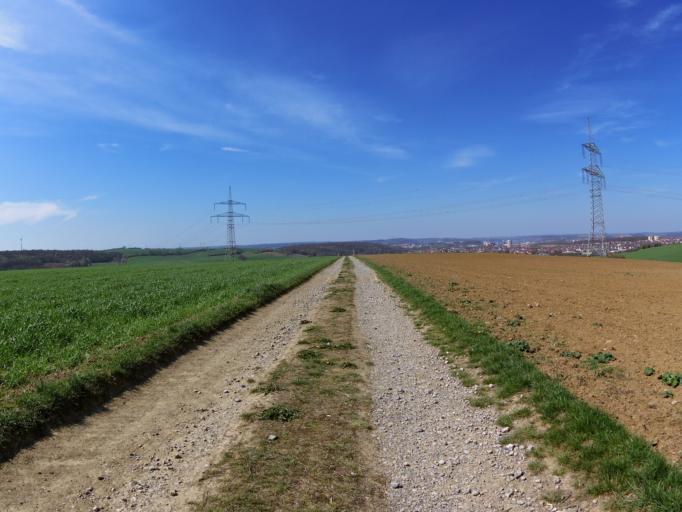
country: DE
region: Bavaria
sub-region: Regierungsbezirk Unterfranken
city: Rottendorf
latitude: 49.7878
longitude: 10.0552
